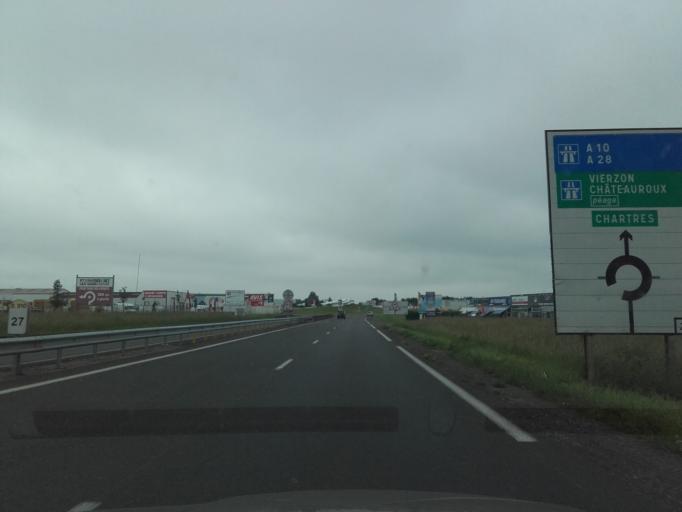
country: FR
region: Centre
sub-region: Departement d'Indre-et-Loire
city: Parcay-Meslay
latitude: 47.4469
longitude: 0.7244
